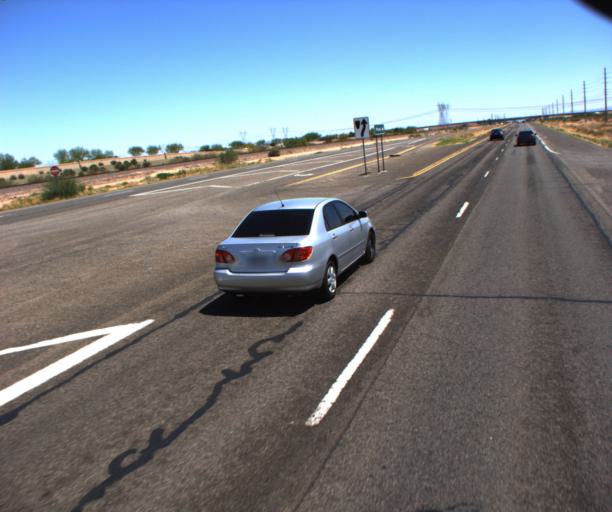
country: US
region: Arizona
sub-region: Maricopa County
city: Sun City West
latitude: 33.6913
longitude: -112.4180
